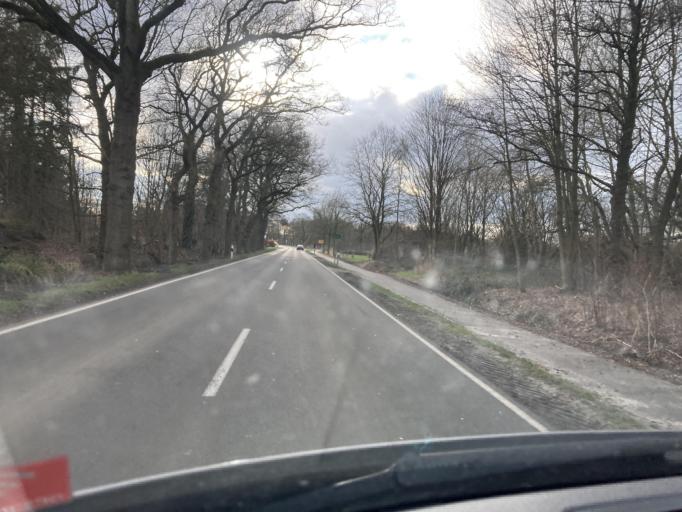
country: DE
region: Lower Saxony
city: Ostrhauderfehn
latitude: 53.1604
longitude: 7.5576
